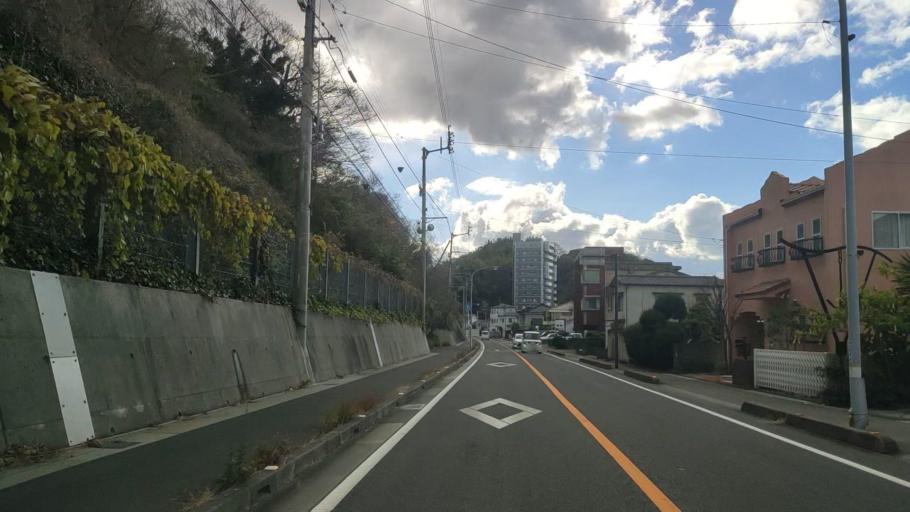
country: JP
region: Ehime
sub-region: Shikoku-chuo Shi
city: Matsuyama
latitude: 33.8722
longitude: 132.7096
